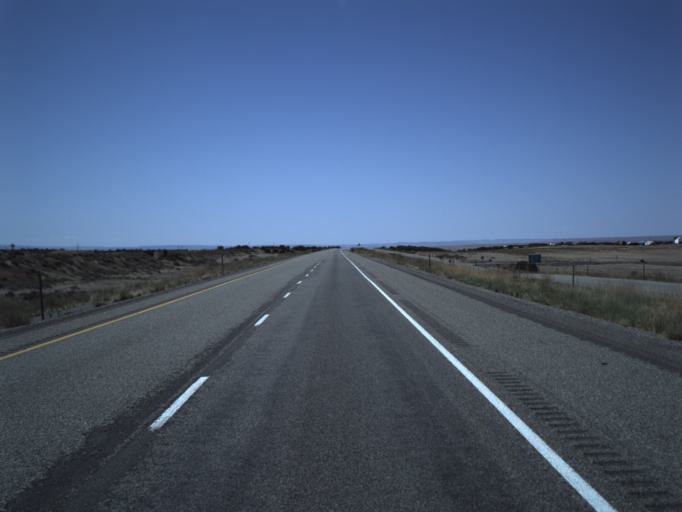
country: US
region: Colorado
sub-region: Mesa County
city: Loma
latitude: 39.1773
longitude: -109.1251
